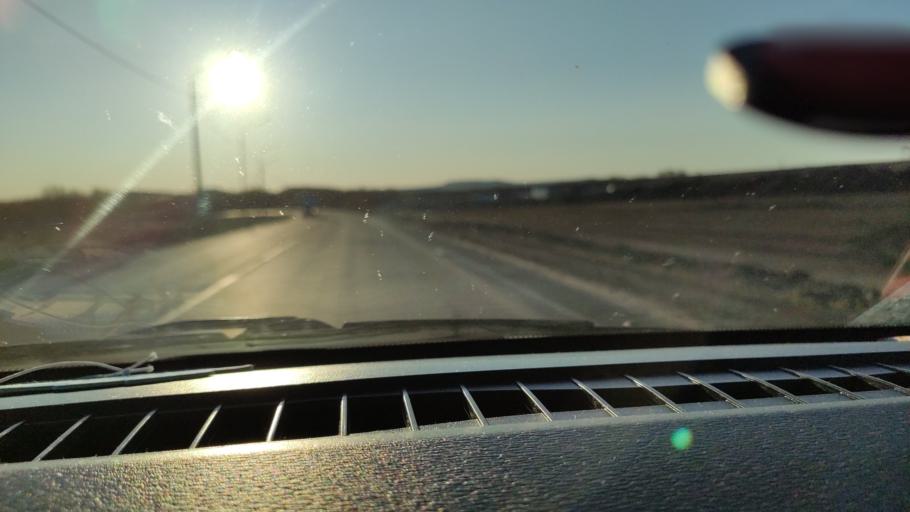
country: RU
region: Saratov
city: Sennoy
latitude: 52.1585
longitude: 47.0734
